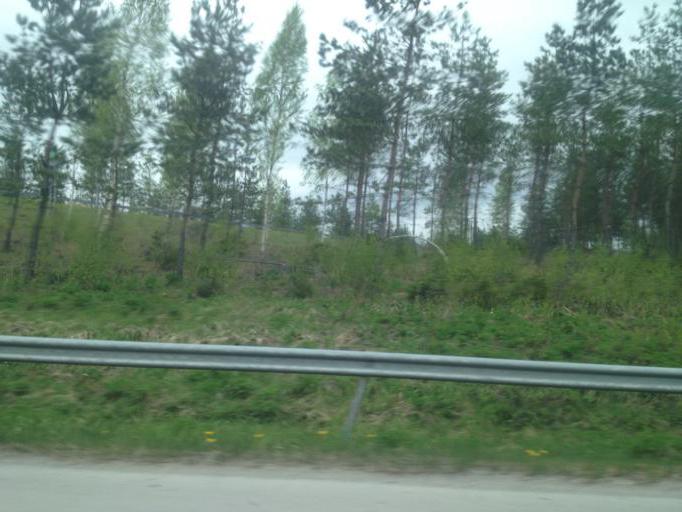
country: FI
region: Uusimaa
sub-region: Helsinki
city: Hyvinge
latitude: 60.5519
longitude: 24.8352
